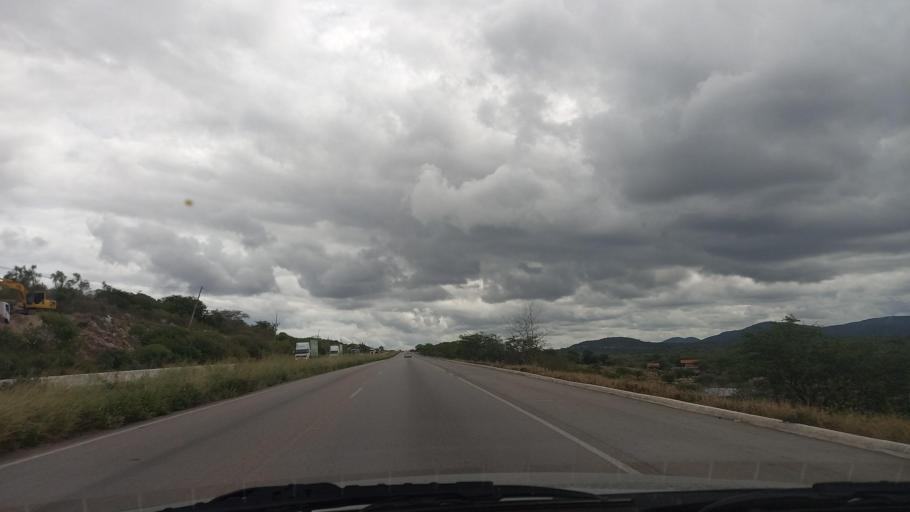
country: BR
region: Pernambuco
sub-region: Caruaru
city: Caruaru
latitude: -8.3224
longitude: -36.0949
